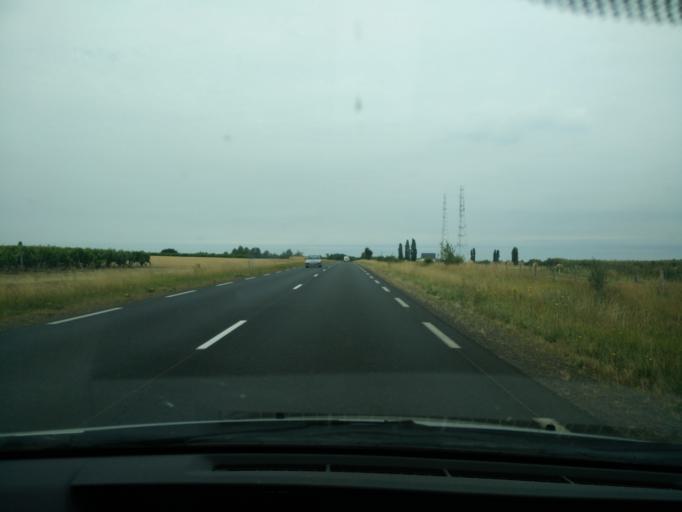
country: FR
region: Pays de la Loire
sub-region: Departement de Maine-et-Loire
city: Doue-la-Fontaine
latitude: 47.1803
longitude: -0.2759
